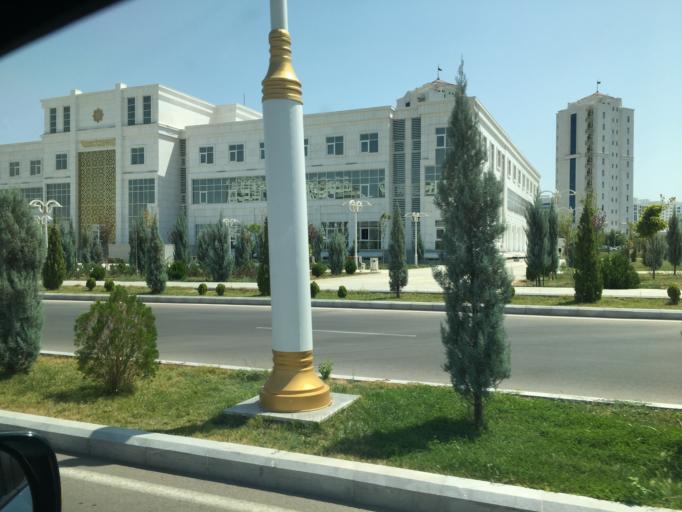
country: TM
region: Ahal
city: Ashgabat
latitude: 37.9155
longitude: 58.3678
